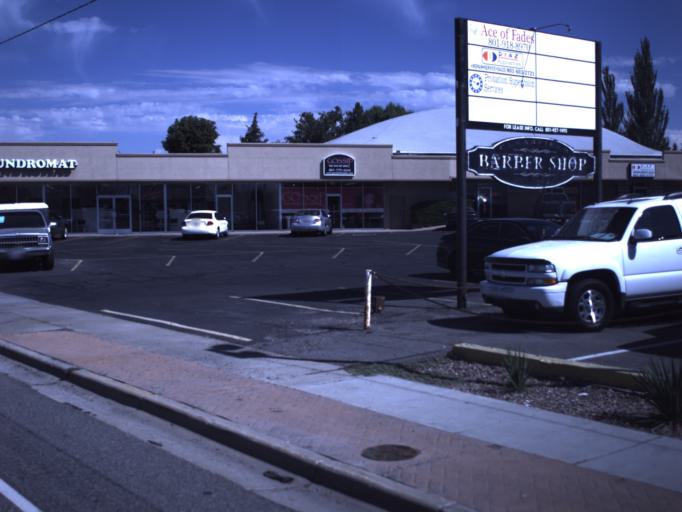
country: US
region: Utah
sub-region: Davis County
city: Clearfield
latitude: 41.1058
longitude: -112.0177
